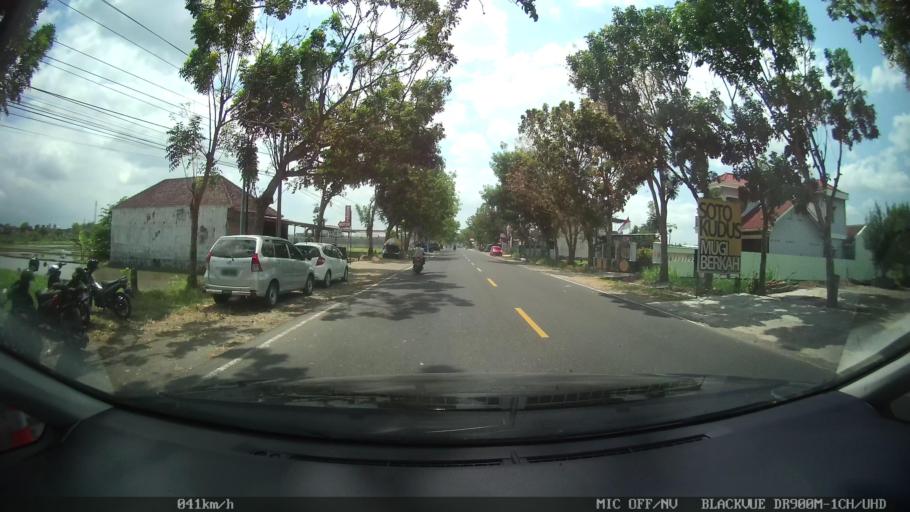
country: ID
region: Daerah Istimewa Yogyakarta
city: Bantul
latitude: -7.9039
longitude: 110.3454
